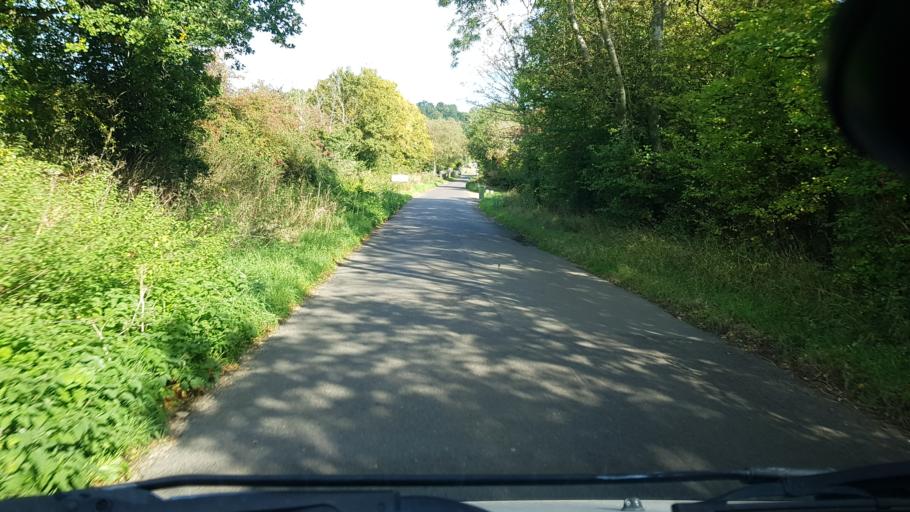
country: GB
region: England
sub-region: Surrey
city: Shalford
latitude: 51.2148
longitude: -0.5962
